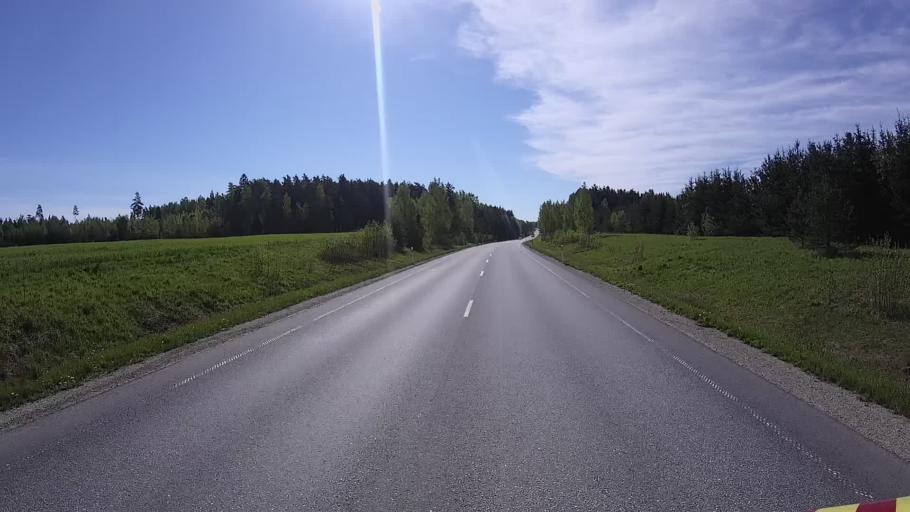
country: EE
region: Tartu
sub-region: Tartu linn
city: Tartu
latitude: 58.3494
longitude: 26.9329
